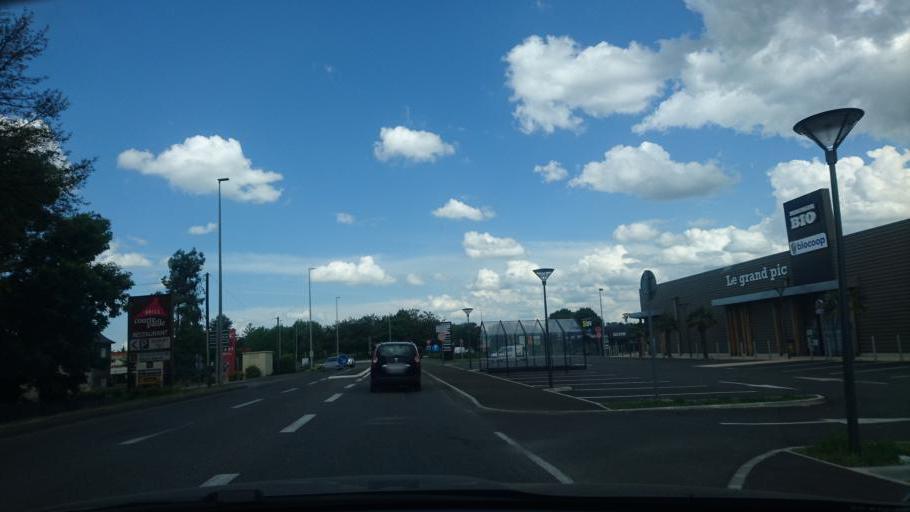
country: FR
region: Midi-Pyrenees
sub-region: Departement des Hautes-Pyrenees
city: Ibos
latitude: 43.2381
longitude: 0.0402
